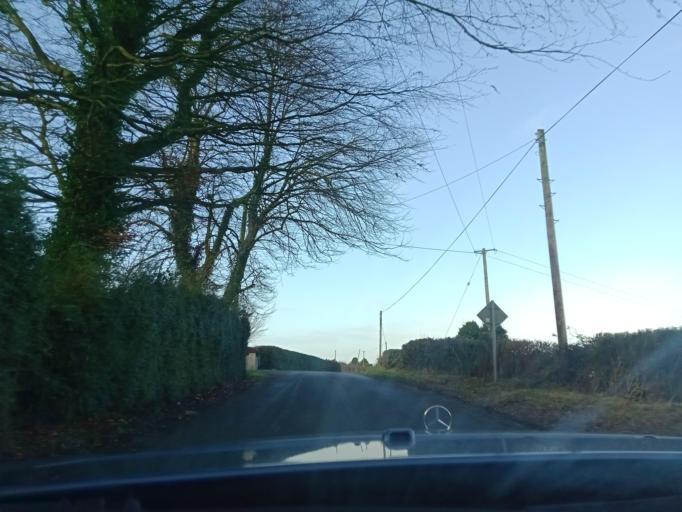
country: IE
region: Leinster
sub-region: Kilkenny
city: Callan
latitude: 52.4730
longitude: -7.4248
